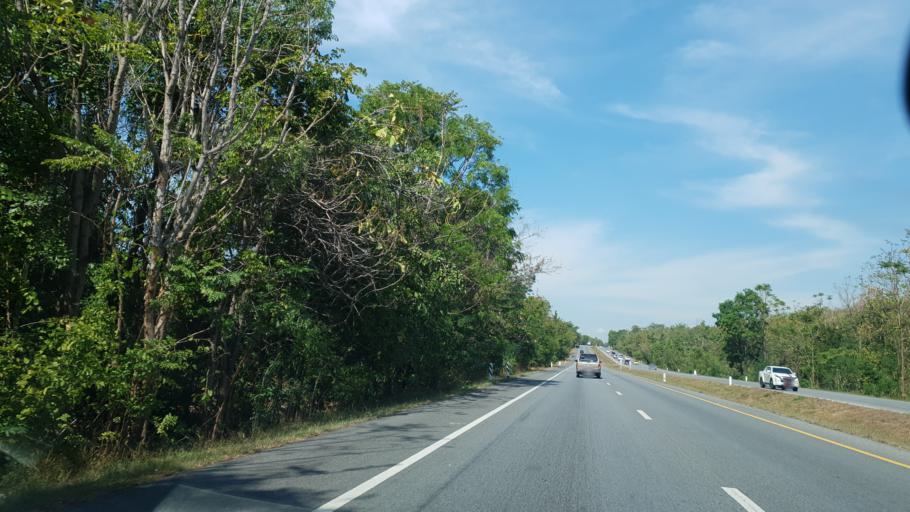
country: TH
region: Uttaradit
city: Thong Saen Khan
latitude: 17.4157
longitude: 100.2276
